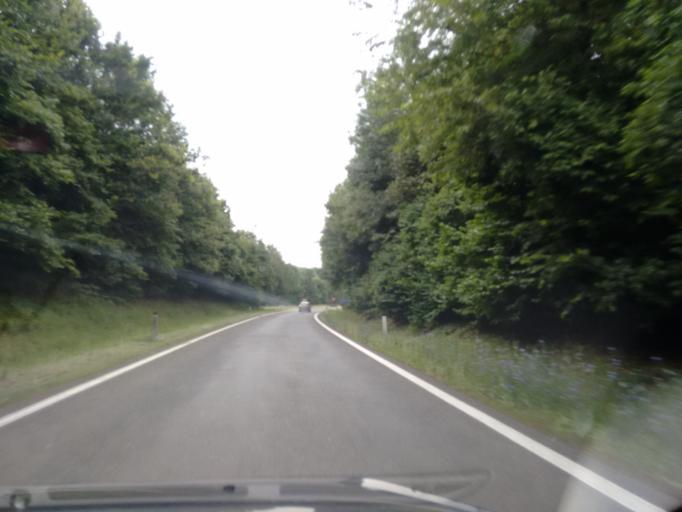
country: AT
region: Upper Austria
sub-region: Politischer Bezirk Grieskirchen
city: Bad Schallerbach
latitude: 48.1903
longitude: 13.9284
